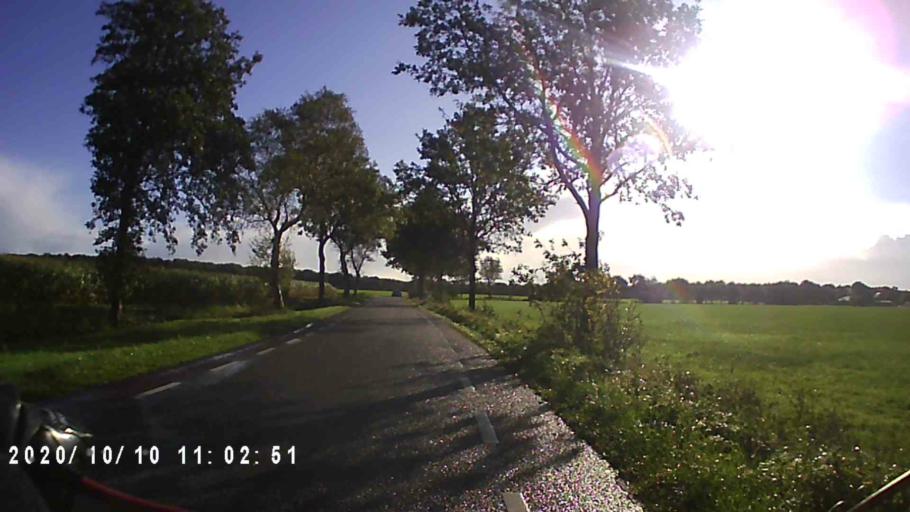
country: NL
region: Friesland
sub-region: Gemeente Achtkarspelen
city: Surhuisterveen
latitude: 53.1358
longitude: 6.2200
